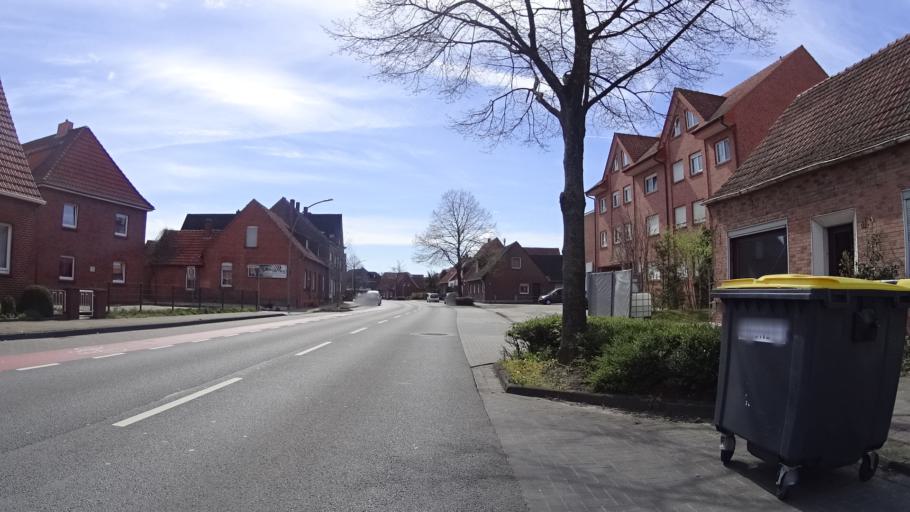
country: DE
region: Lower Saxony
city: Lingen
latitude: 52.5099
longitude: 7.3186
